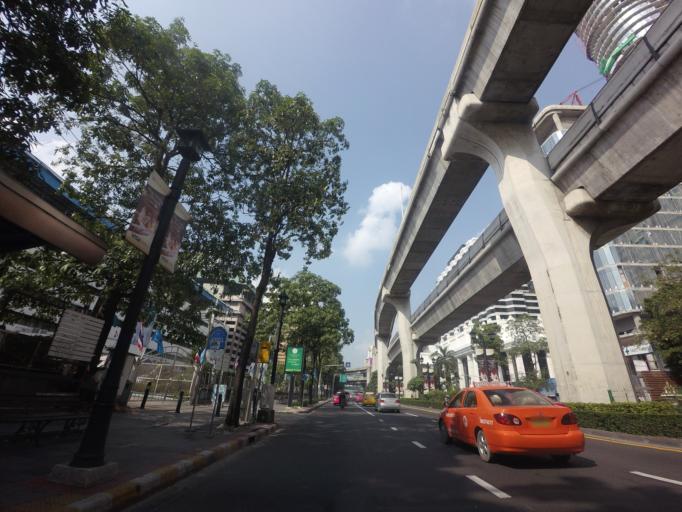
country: TH
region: Bangkok
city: Pathum Wan
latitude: 13.7421
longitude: 100.5397
